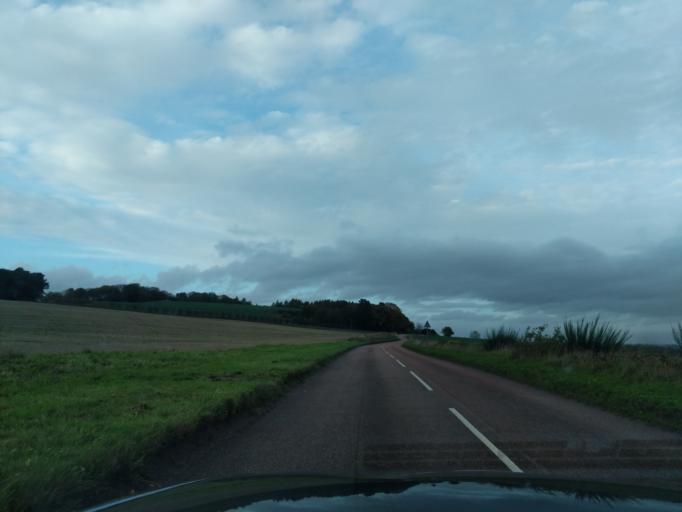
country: GB
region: Scotland
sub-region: Fife
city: Tayport
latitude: 56.4247
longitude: -2.8883
